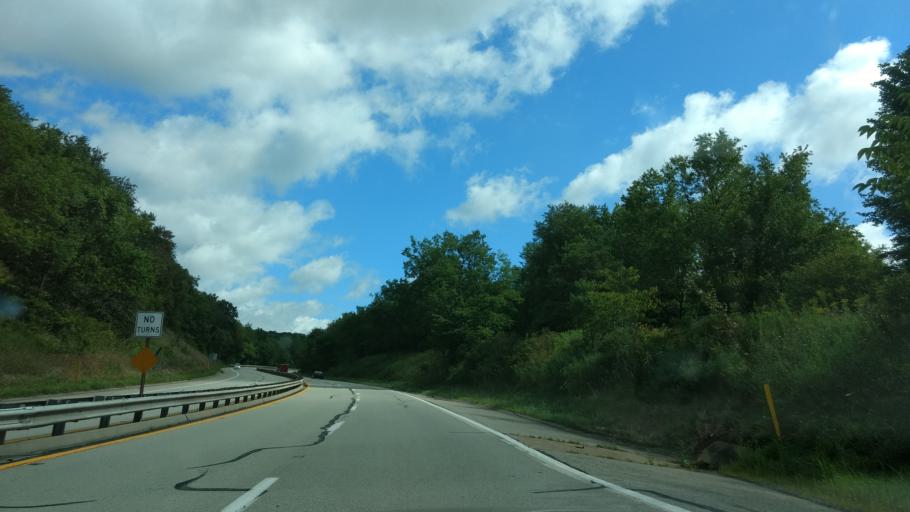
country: US
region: Pennsylvania
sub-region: Westmoreland County
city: Murrysville
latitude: 40.5139
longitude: -79.6449
